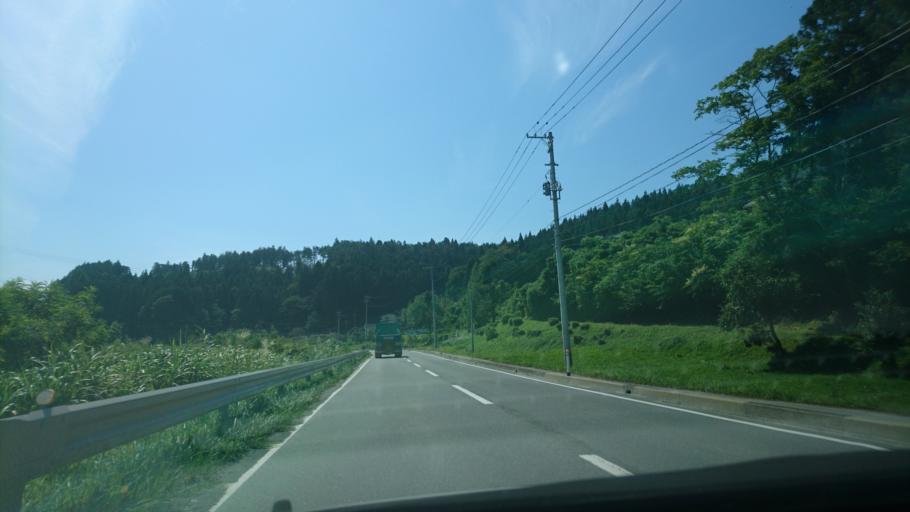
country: JP
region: Iwate
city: Ofunato
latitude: 39.0328
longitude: 141.5993
